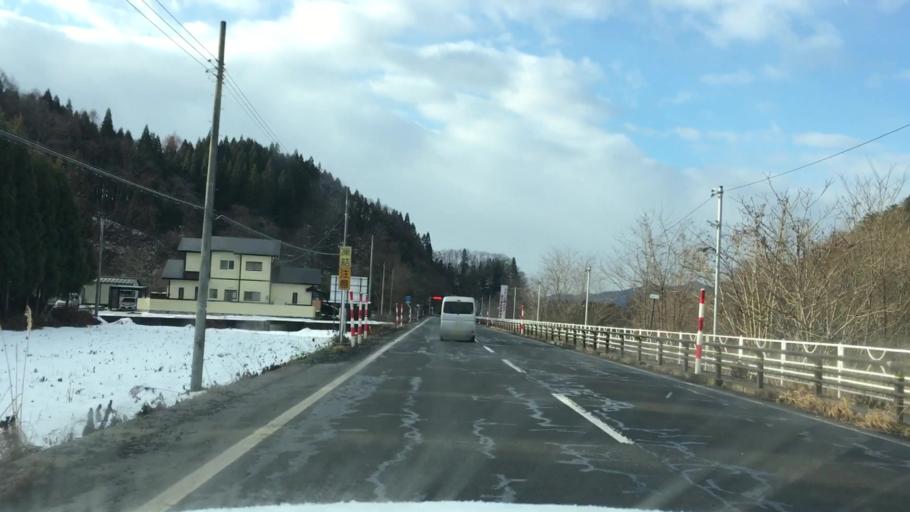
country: JP
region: Akita
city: Odate
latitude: 40.3363
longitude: 140.5883
